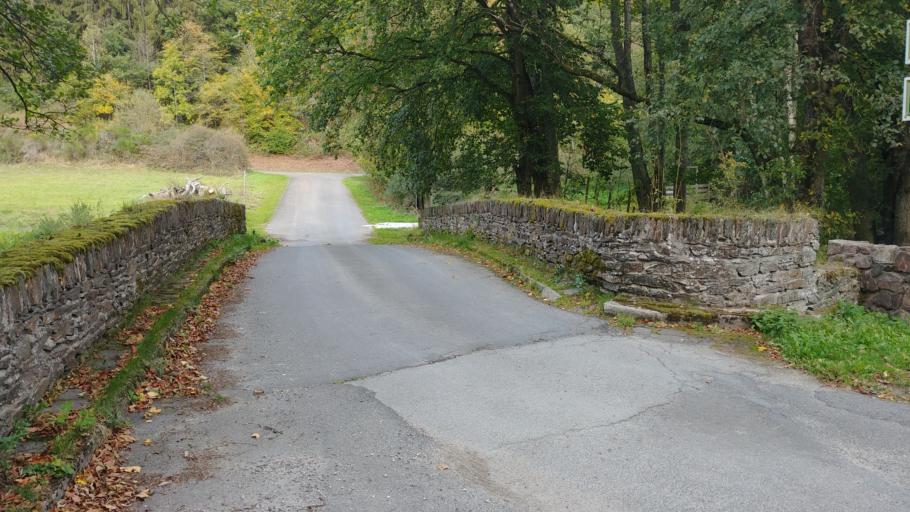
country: DE
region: Rheinland-Pfalz
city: Berglicht
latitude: 49.7963
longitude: 6.9761
